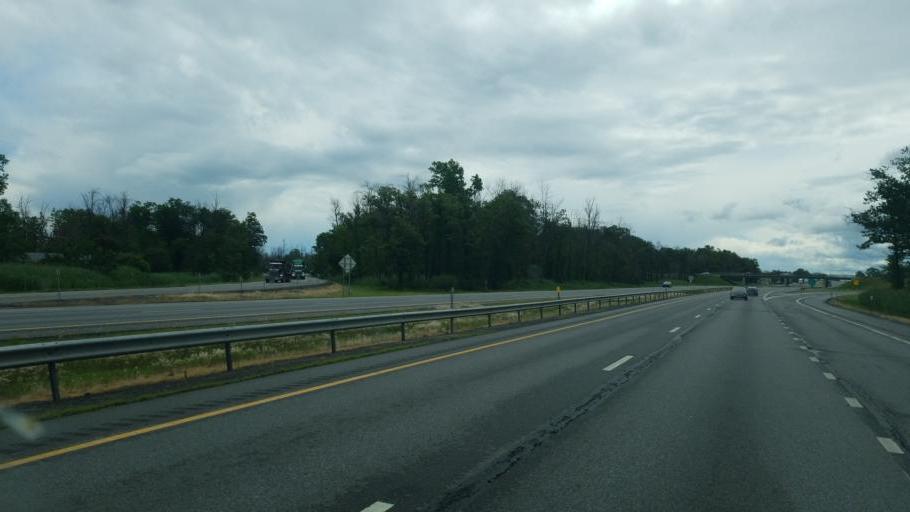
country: US
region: New York
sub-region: Erie County
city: Williamsville
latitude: 42.9507
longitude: -78.7086
